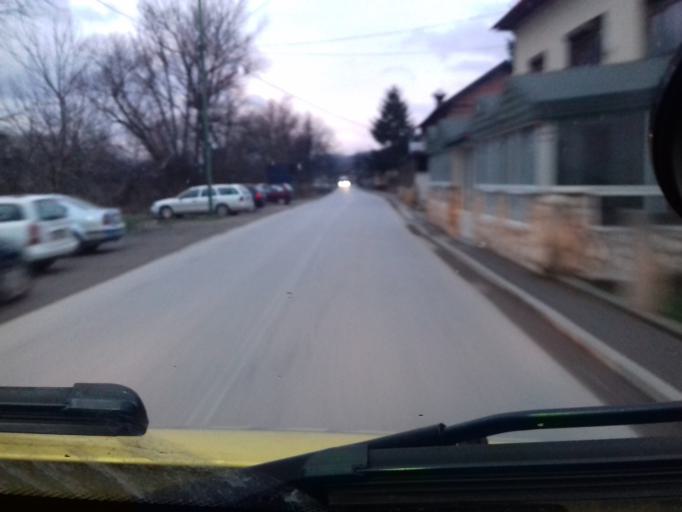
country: BA
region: Federation of Bosnia and Herzegovina
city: Visoko
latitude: 43.9939
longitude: 18.1842
